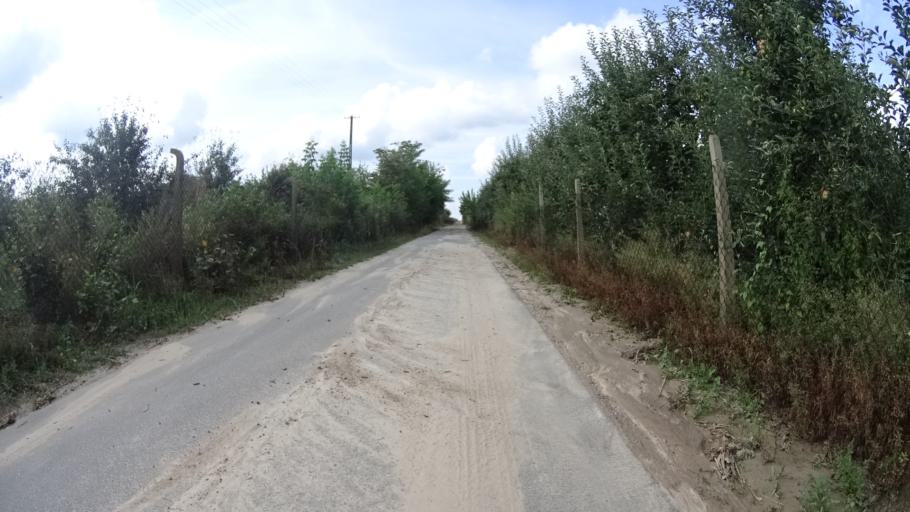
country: PL
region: Masovian Voivodeship
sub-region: Powiat grojecki
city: Goszczyn
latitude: 51.7017
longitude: 20.8156
